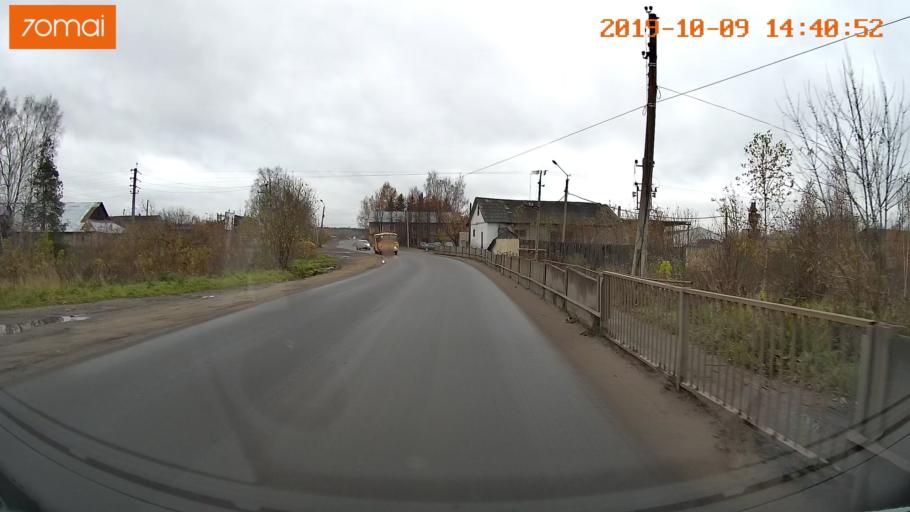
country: RU
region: Kostroma
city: Buy
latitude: 58.4746
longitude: 41.5283
